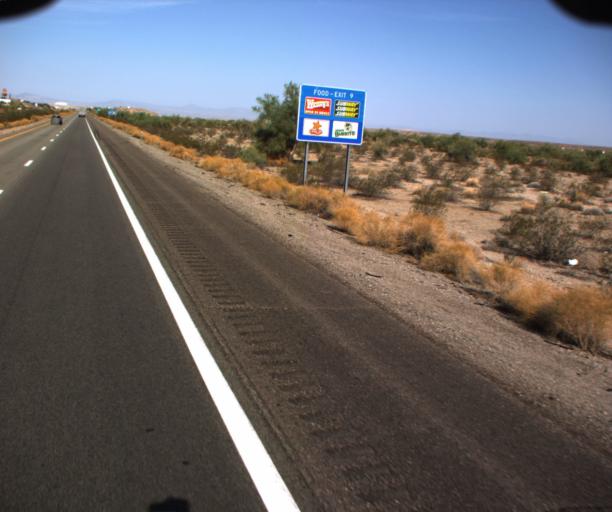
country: US
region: Arizona
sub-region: Mohave County
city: Desert Hills
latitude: 34.7301
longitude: -114.3043
